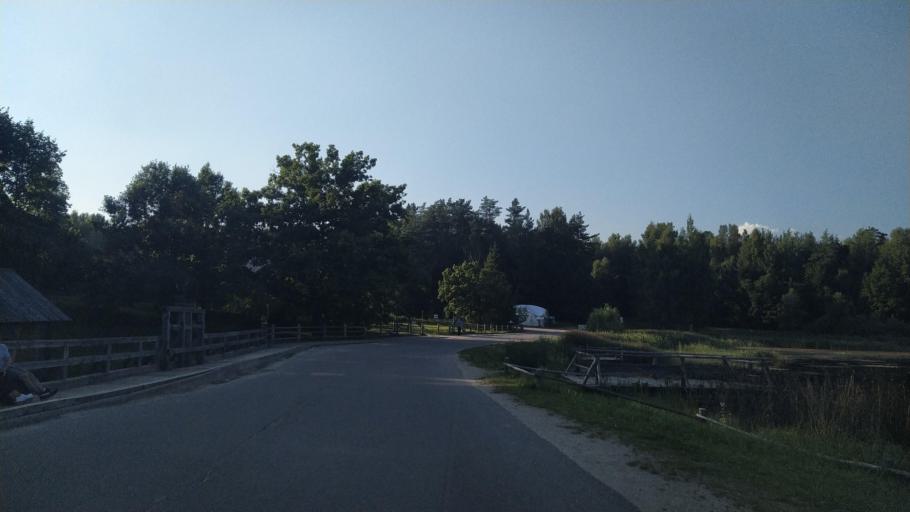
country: RU
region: Pskov
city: Pushkinskiye Gory
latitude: 57.0464
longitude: 28.9178
